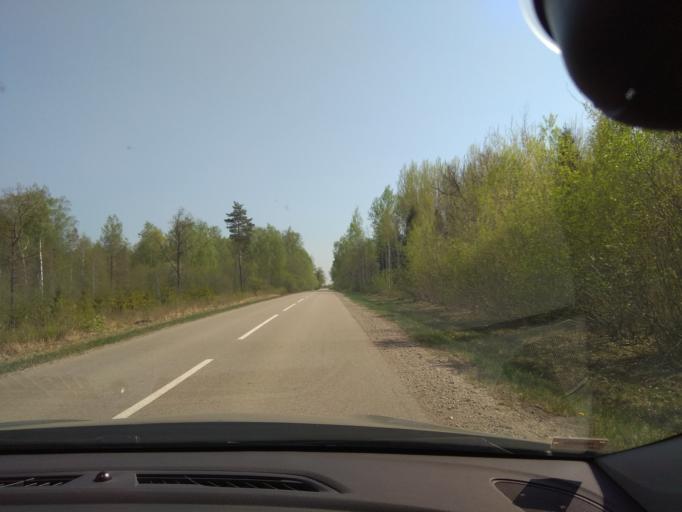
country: LT
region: Panevezys
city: Pasvalys
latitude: 55.9737
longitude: 24.2001
